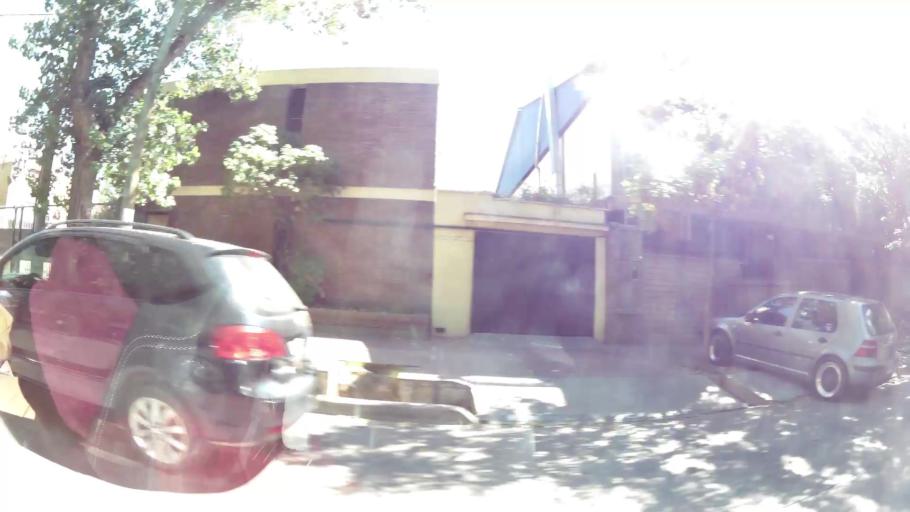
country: AR
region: Mendoza
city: Mendoza
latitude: -32.9034
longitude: -68.8593
